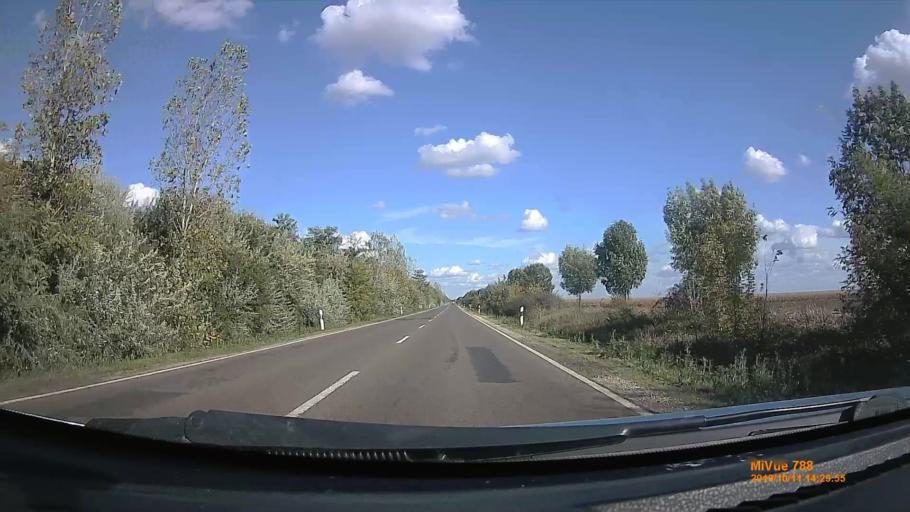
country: HU
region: Hajdu-Bihar
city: Balmazujvaros
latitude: 47.5595
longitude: 21.3910
